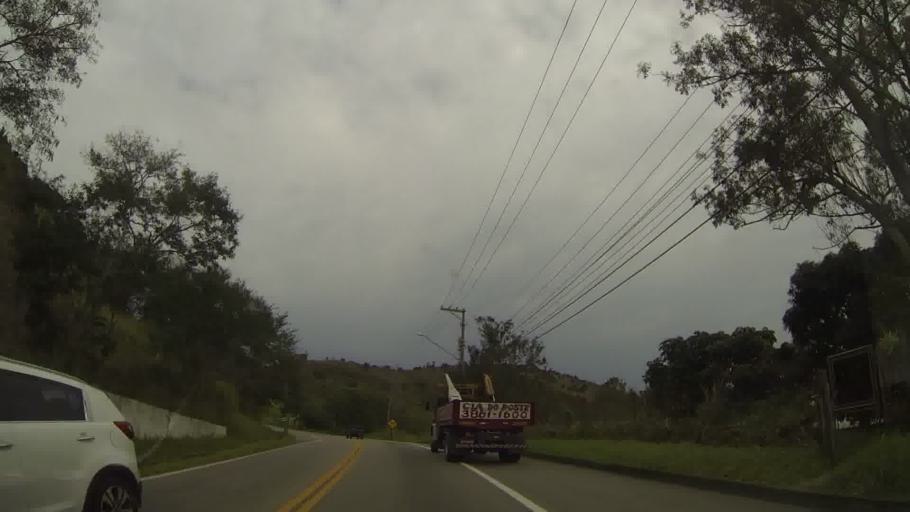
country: BR
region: Sao Paulo
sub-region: Sao Sebastiao
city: Sao Sebastiao
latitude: -23.8254
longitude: -45.5293
